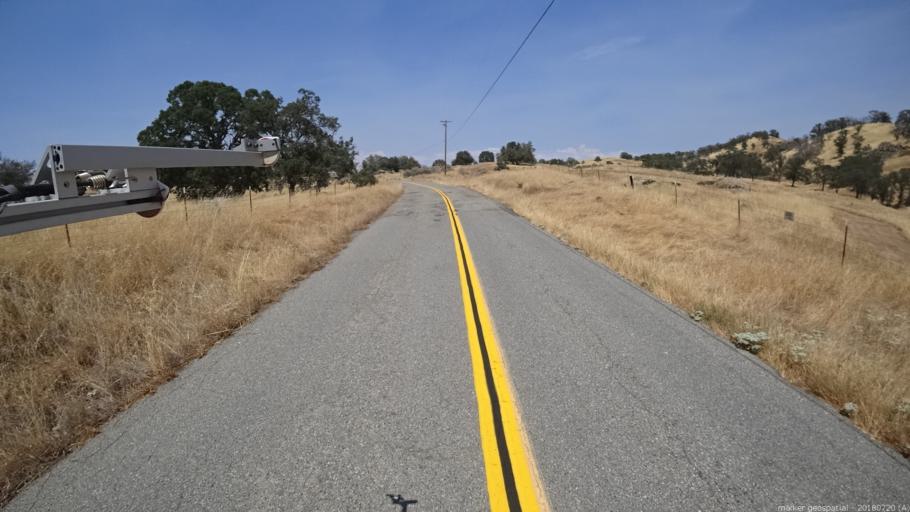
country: US
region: California
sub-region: Madera County
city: Yosemite Lakes
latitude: 37.1294
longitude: -119.8529
